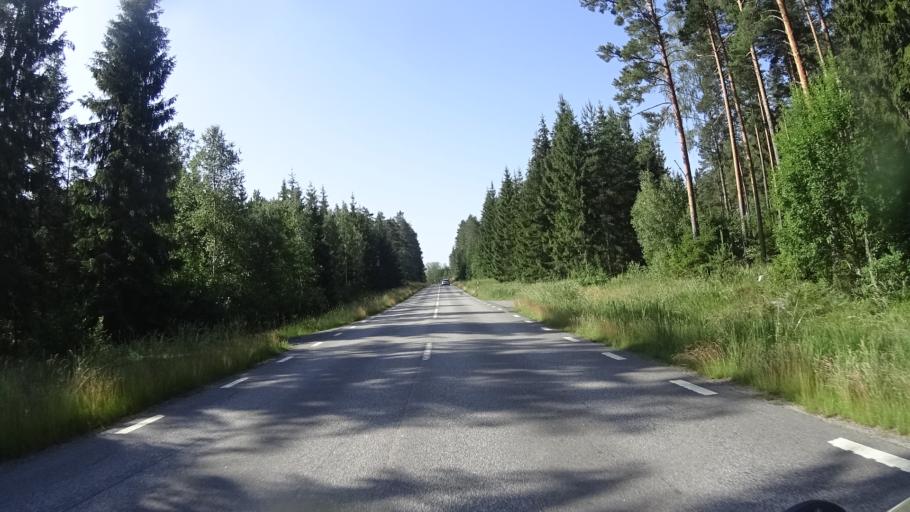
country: SE
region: OEstergoetland
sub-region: Atvidabergs Kommun
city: Atvidaberg
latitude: 58.1264
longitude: 16.0933
